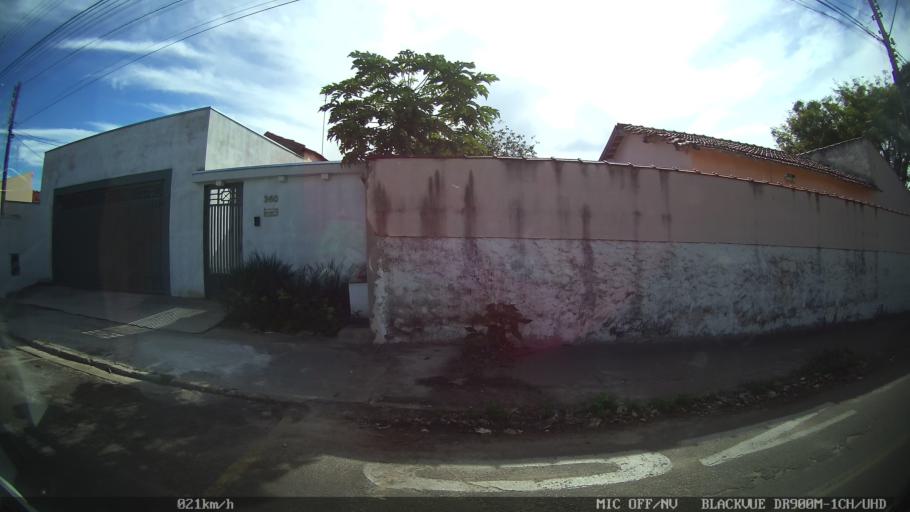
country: BR
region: Sao Paulo
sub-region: Catanduva
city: Catanduva
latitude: -21.1154
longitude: -48.9674
